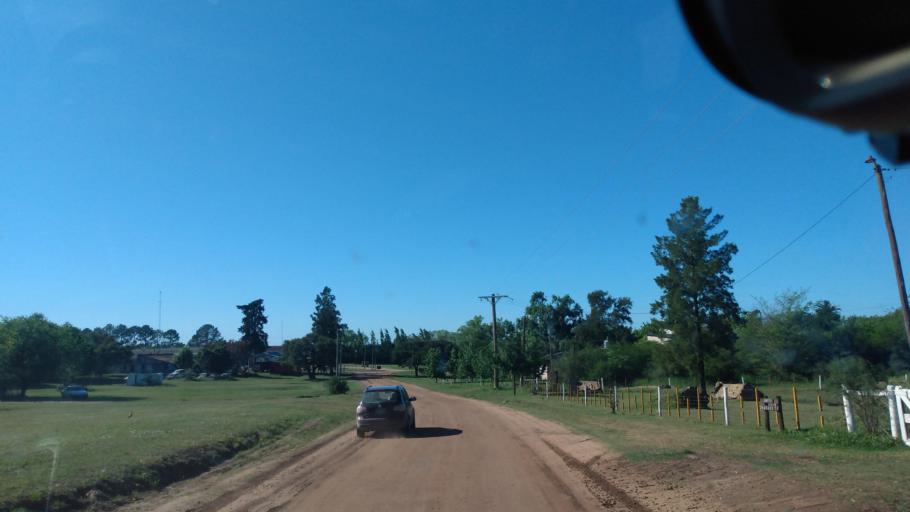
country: AR
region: Entre Rios
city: Colon
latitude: -32.1534
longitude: -58.1964
